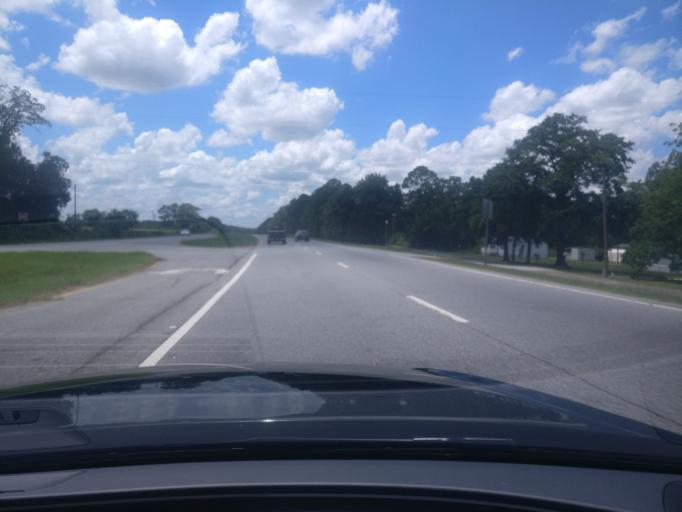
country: US
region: Georgia
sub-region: Worth County
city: Sylvester
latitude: 31.5109
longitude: -83.7568
